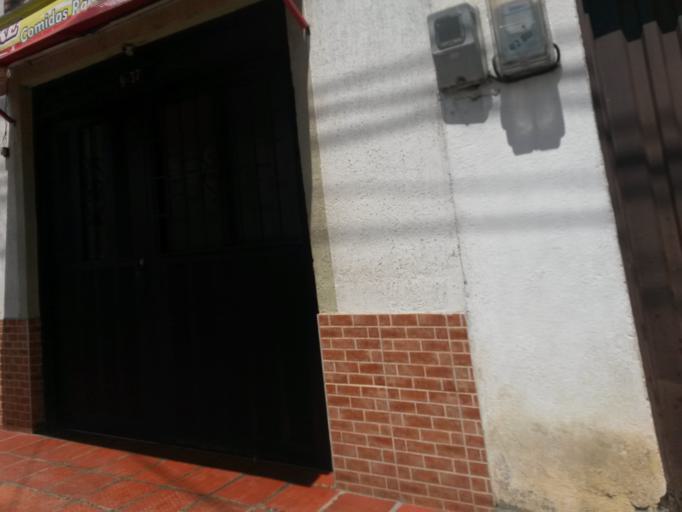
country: CO
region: Cauca
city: Santander de Quilichao
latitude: 3.0087
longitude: -76.4817
